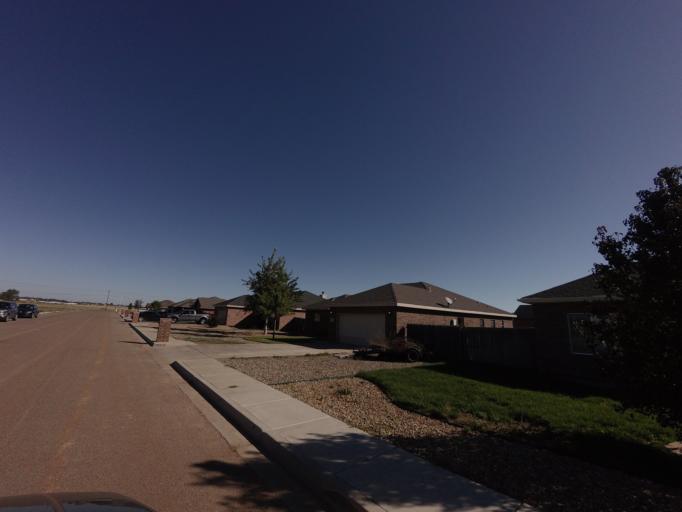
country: US
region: New Mexico
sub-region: Curry County
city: Clovis
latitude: 34.4322
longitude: -103.1690
